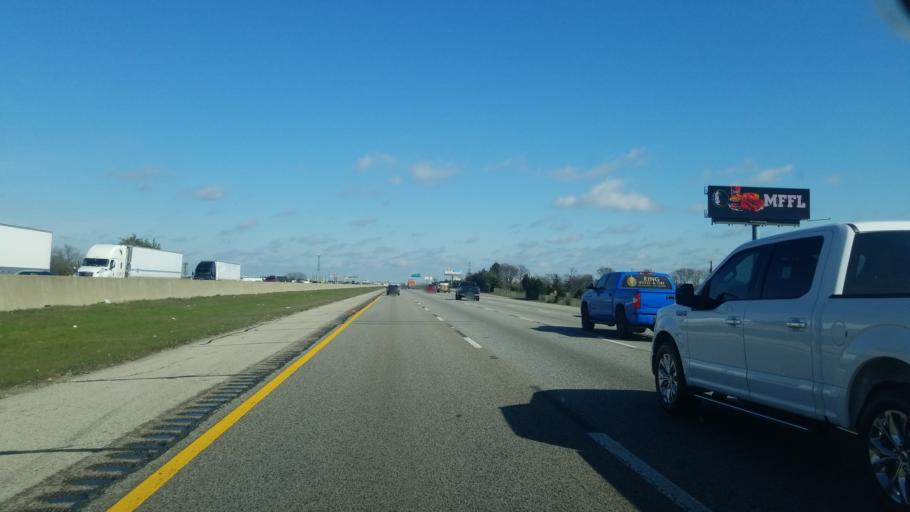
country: US
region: Texas
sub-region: Dallas County
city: Hutchins
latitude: 32.6503
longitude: -96.7704
